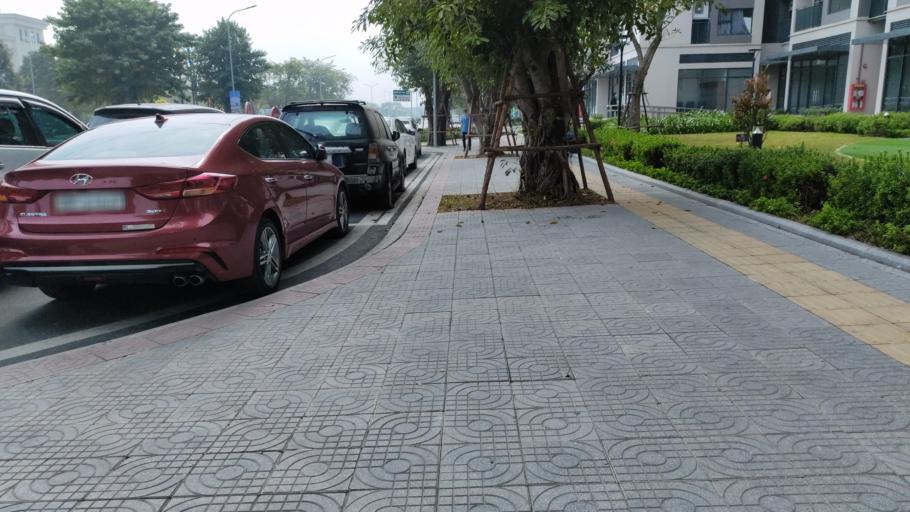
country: VN
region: Ha Noi
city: Trau Quy
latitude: 20.9906
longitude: 105.9434
